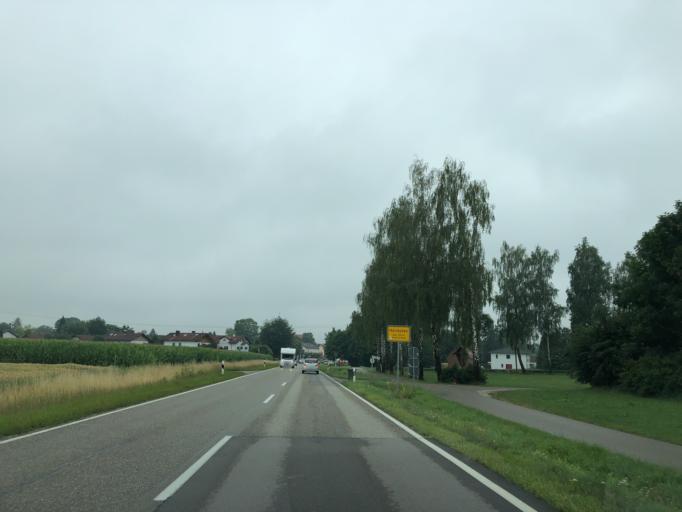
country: DE
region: Bavaria
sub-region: Upper Bavaria
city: Worth
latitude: 48.2462
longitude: 11.9349
